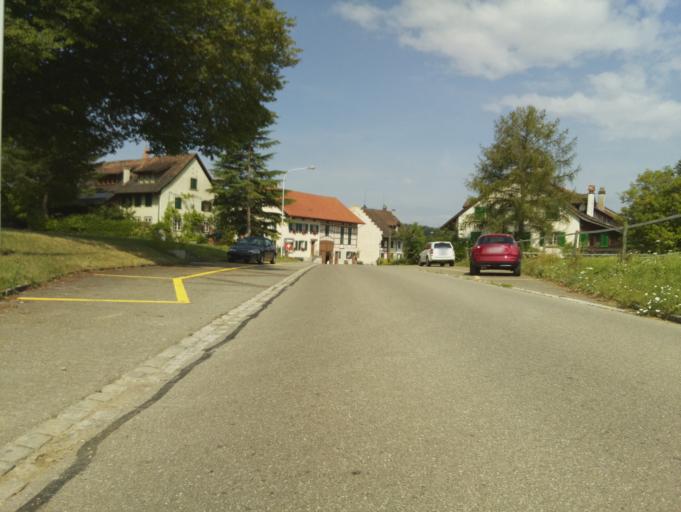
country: CH
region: Zurich
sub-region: Bezirk Andelfingen
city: Henggart
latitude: 47.5760
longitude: 8.6730
